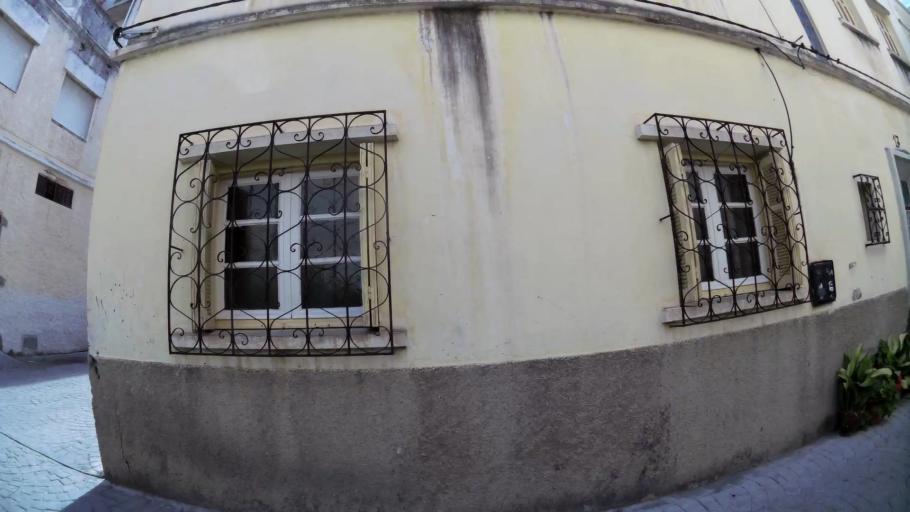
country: MA
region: Tanger-Tetouan
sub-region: Tanger-Assilah
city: Tangier
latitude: 35.7623
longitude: -5.8052
